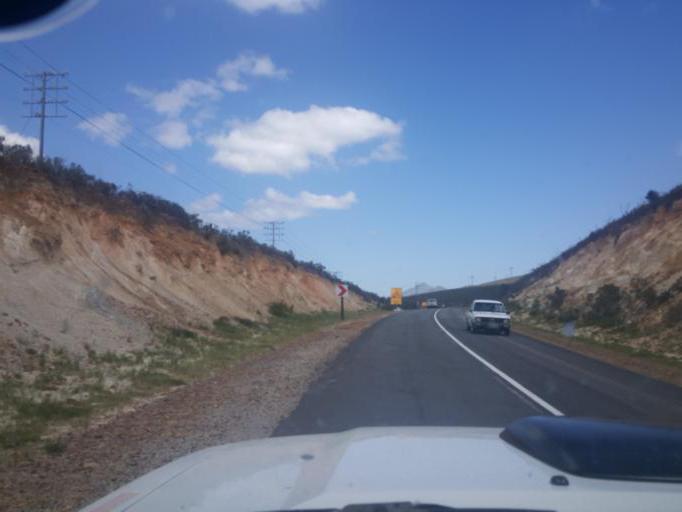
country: ZA
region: Eastern Cape
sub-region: Cacadu District Municipality
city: Kareedouw
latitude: -33.9557
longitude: 24.3602
